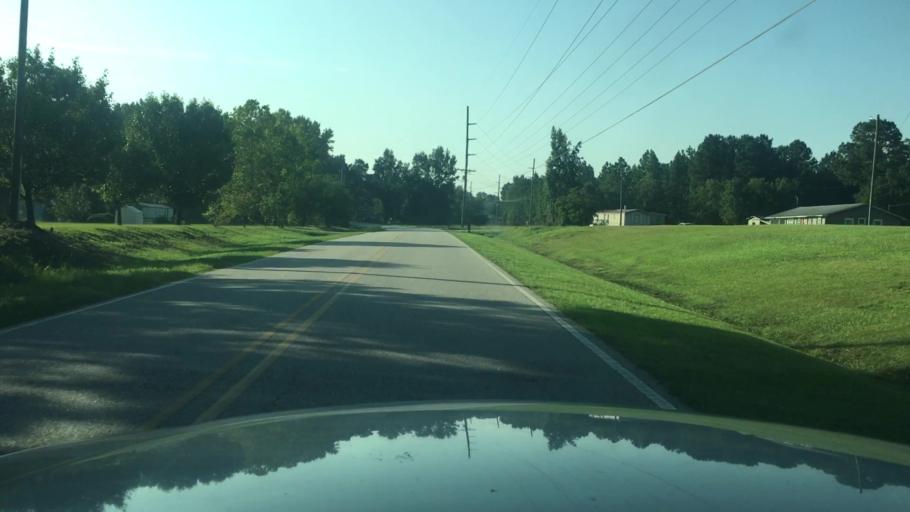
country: US
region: North Carolina
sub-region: Cumberland County
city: Spring Lake
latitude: 35.2089
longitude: -78.8939
